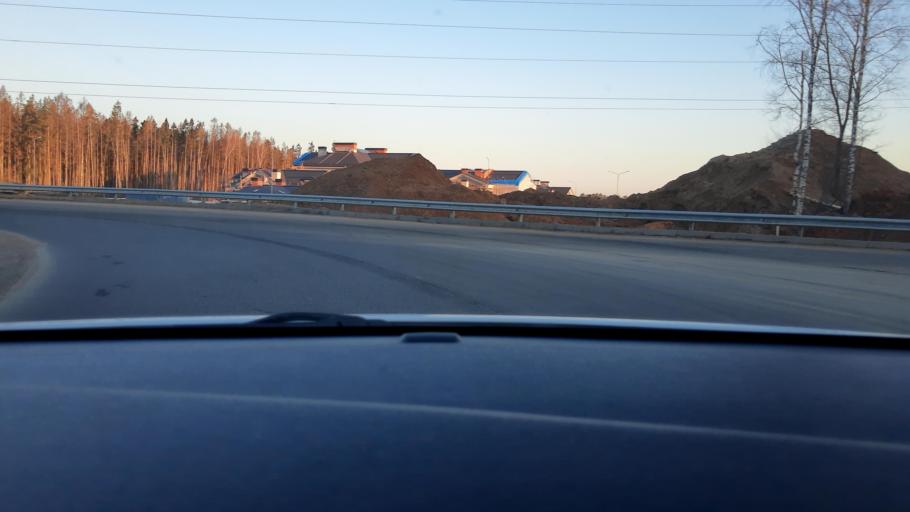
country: RU
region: Moskovskaya
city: Barvikha
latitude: 55.7209
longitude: 37.3169
